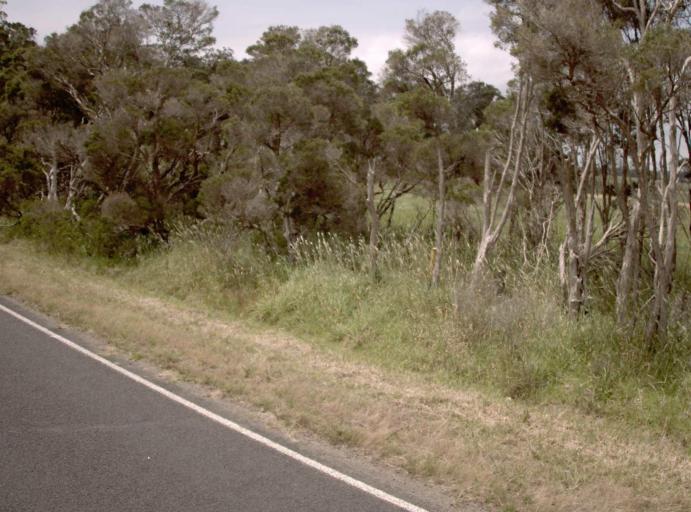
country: AU
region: Victoria
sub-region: Latrobe
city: Traralgon
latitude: -38.5444
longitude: 146.6559
